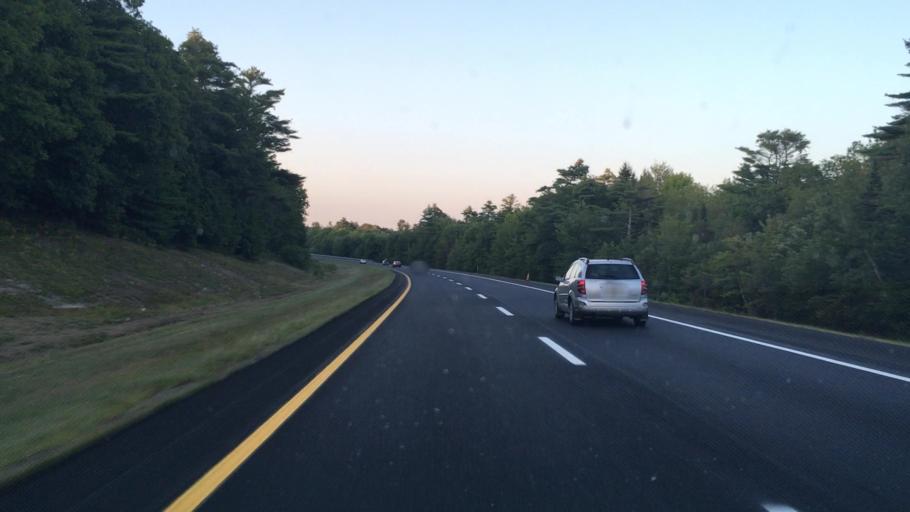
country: US
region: Maine
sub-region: Sagadahoc County
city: Topsham
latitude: 44.0049
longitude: -69.9248
